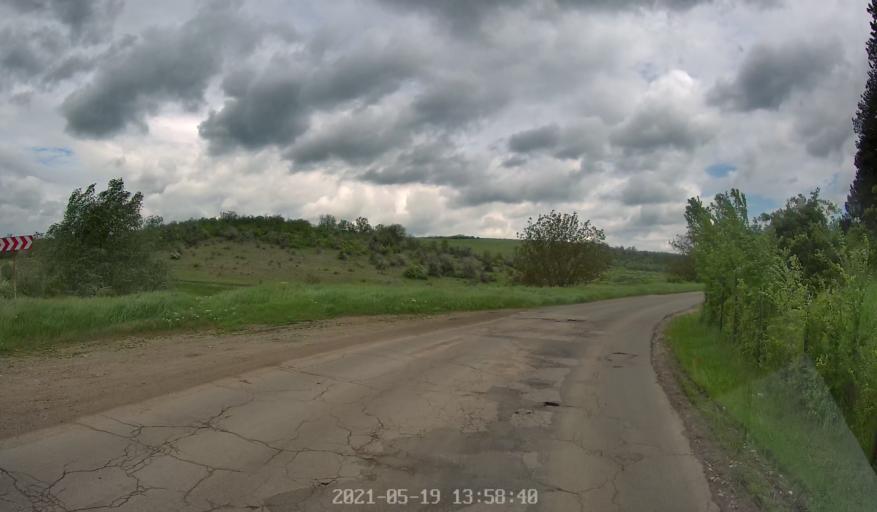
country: MD
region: Chisinau
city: Chisinau
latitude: 47.0431
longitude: 28.9187
